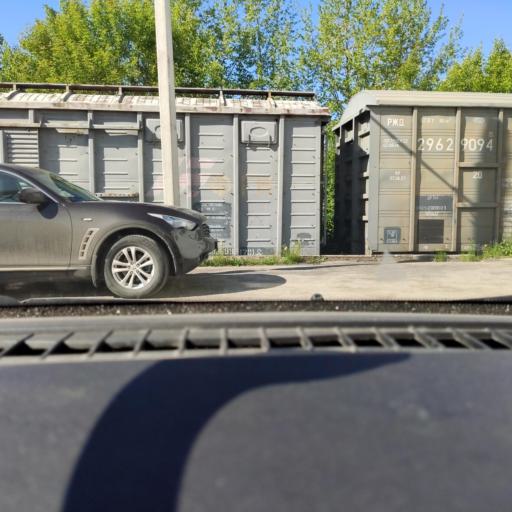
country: RU
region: Perm
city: Froly
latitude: 57.9538
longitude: 56.2514
